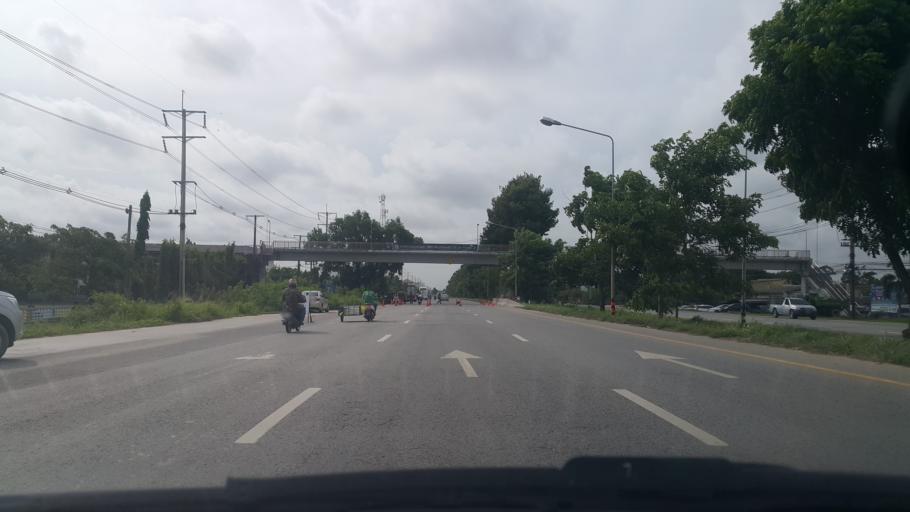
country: TH
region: Rayong
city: Rayong
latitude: 12.6737
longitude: 101.3042
